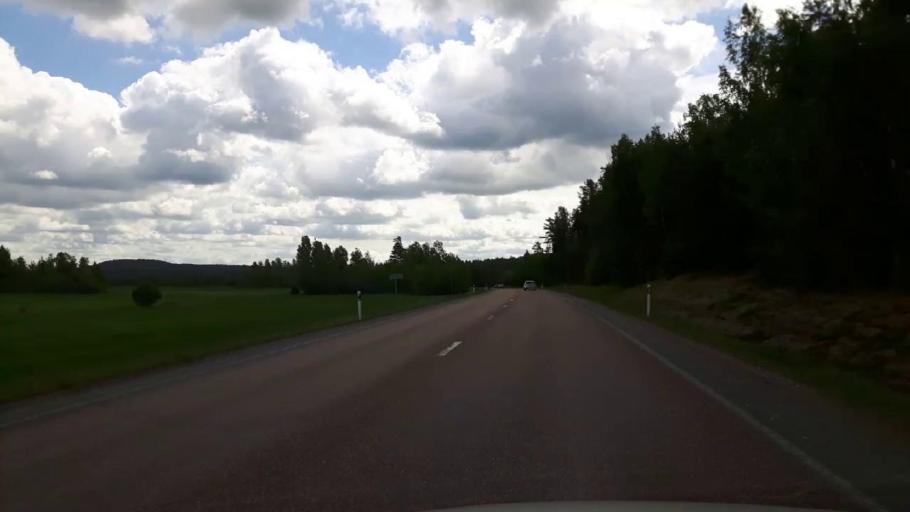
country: SE
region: Dalarna
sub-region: Faluns Kommun
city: Falun
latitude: 60.5055
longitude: 15.7397
